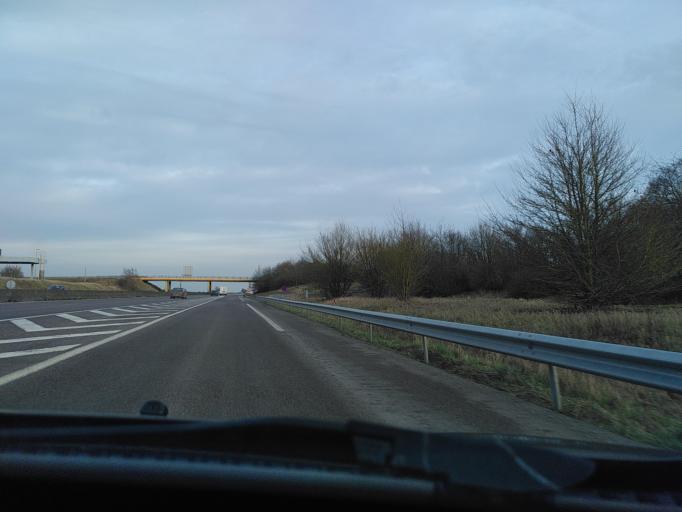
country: FR
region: Picardie
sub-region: Departement de la Somme
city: Villers-Bretonneux
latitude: 49.8536
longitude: 2.5215
